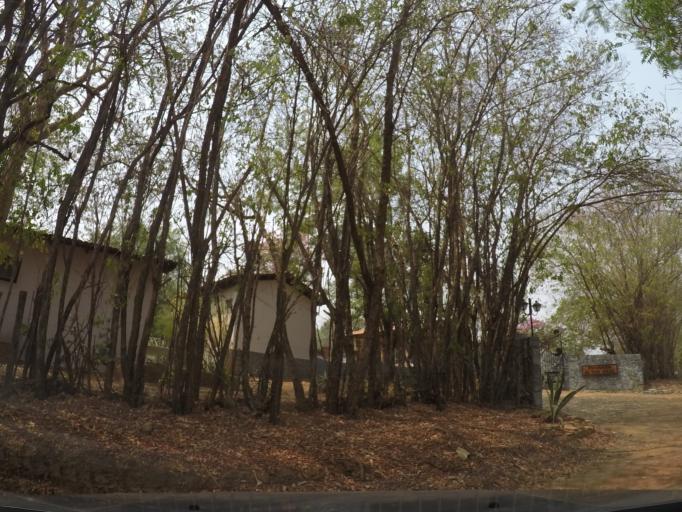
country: BR
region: Goias
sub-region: Pirenopolis
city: Pirenopolis
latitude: -15.8349
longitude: -48.9491
